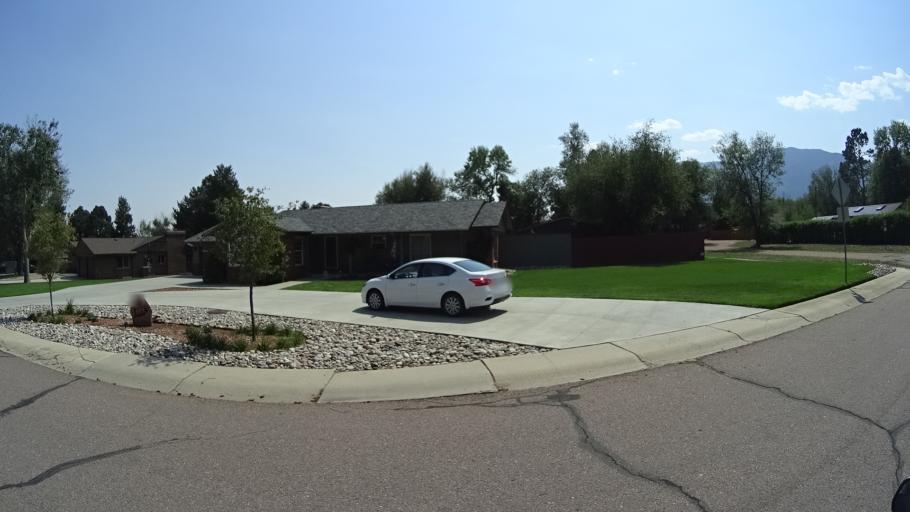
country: US
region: Colorado
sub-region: El Paso County
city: Colorado Springs
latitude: 38.7962
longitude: -104.8323
